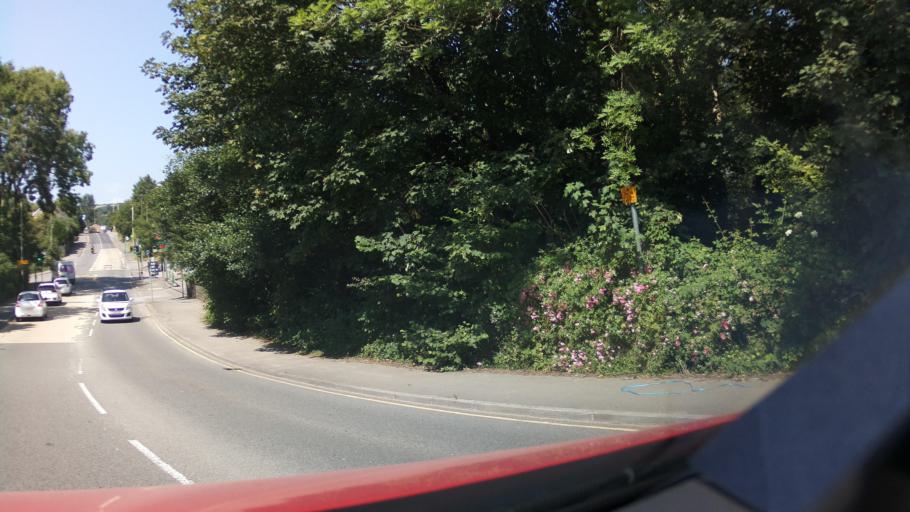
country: GB
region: Wales
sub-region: Caerphilly County Borough
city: Caerphilly
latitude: 51.5819
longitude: -3.2412
